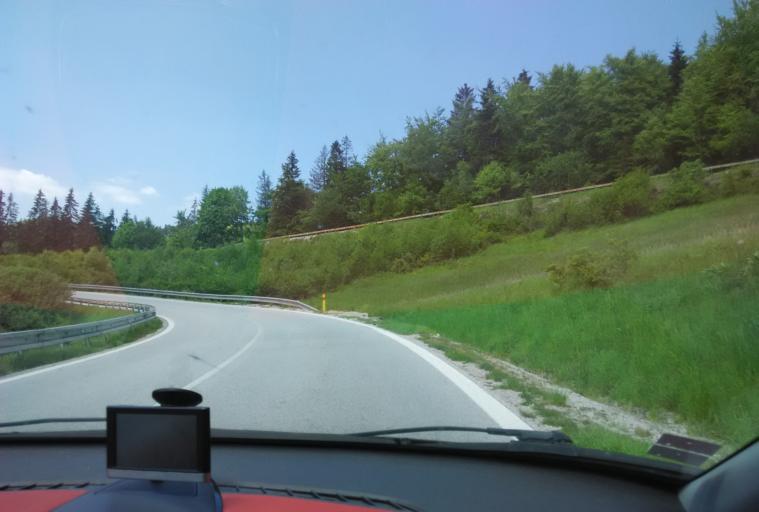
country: SK
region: Kosicky
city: Dobsina
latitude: 48.8463
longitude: 20.3755
